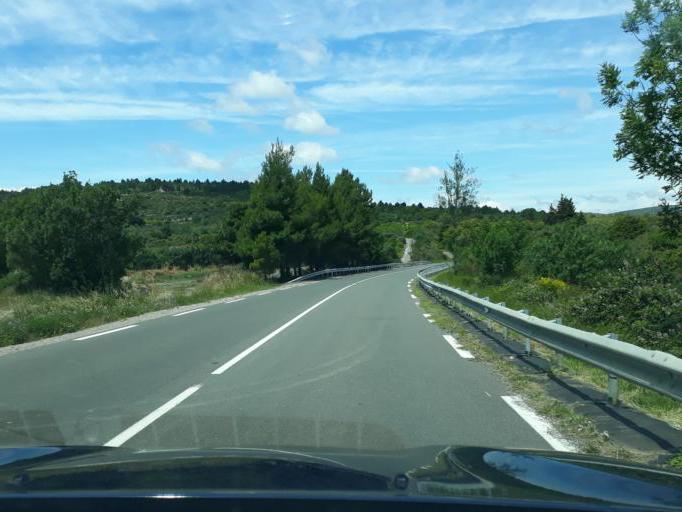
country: FR
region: Languedoc-Roussillon
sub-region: Departement de l'Aude
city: Portel-des-Corbieres
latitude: 43.0426
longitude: 2.9328
